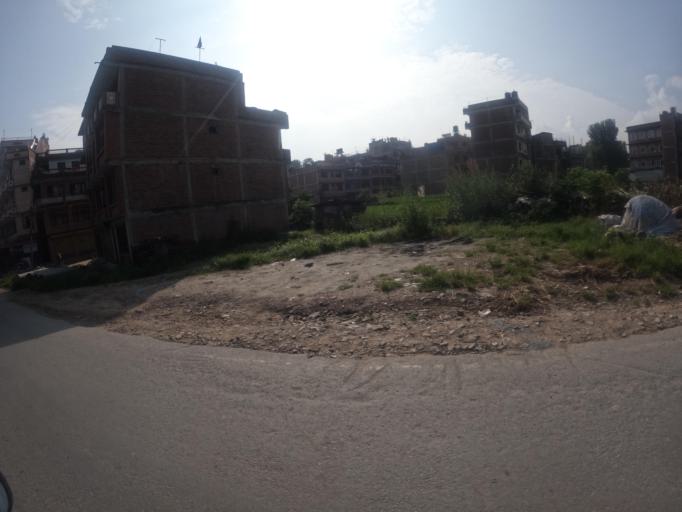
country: NP
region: Central Region
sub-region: Bagmati Zone
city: Bhaktapur
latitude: 27.6794
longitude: 85.4351
